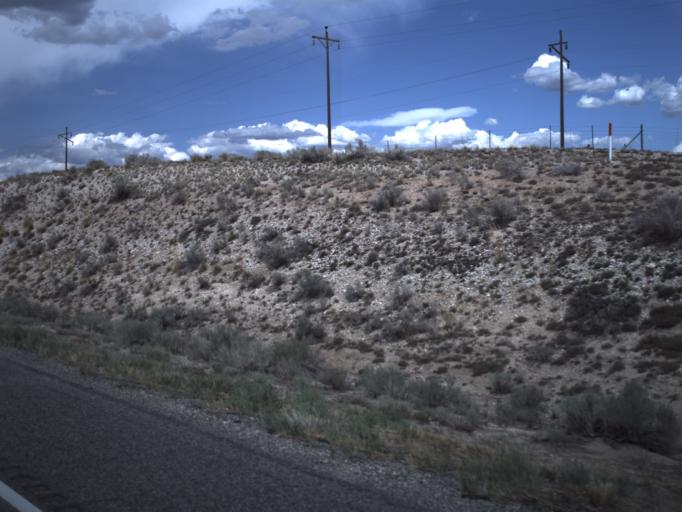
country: US
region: Utah
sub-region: Sevier County
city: Salina
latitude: 39.0147
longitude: -111.8351
